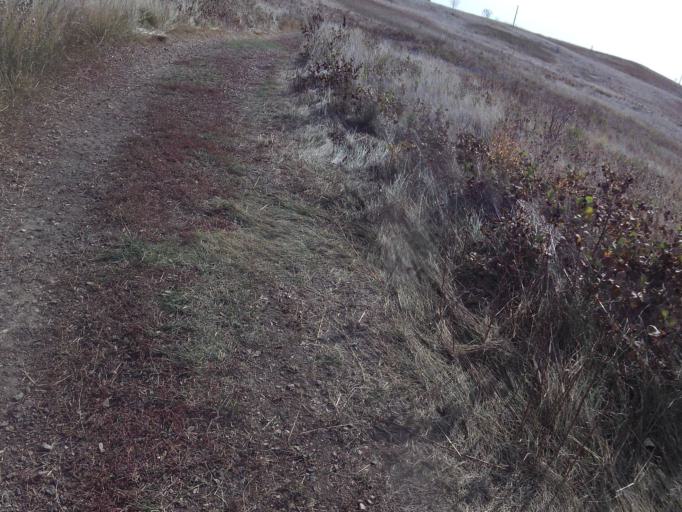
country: CA
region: Manitoba
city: Morden
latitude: 48.9389
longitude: -98.0613
